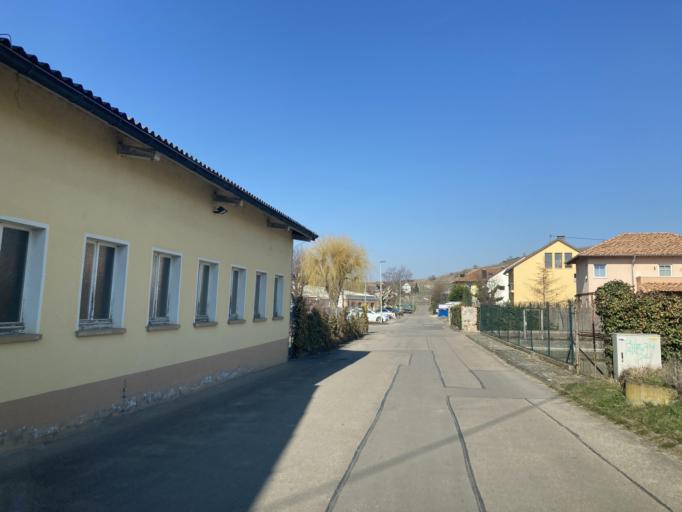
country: DE
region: Baden-Wuerttemberg
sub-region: Freiburg Region
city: Vogtsburg
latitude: 48.1041
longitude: 7.6245
